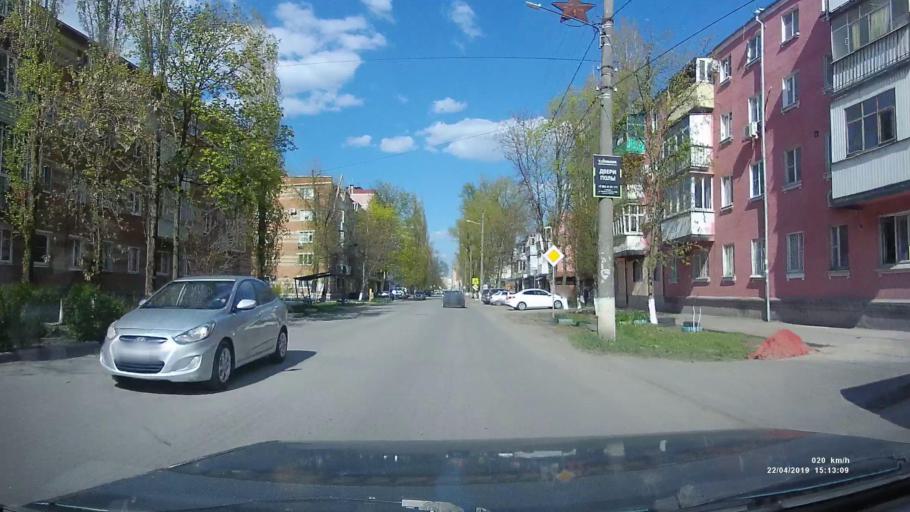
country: RU
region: Rostov
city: Azov
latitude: 47.1016
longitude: 39.4218
